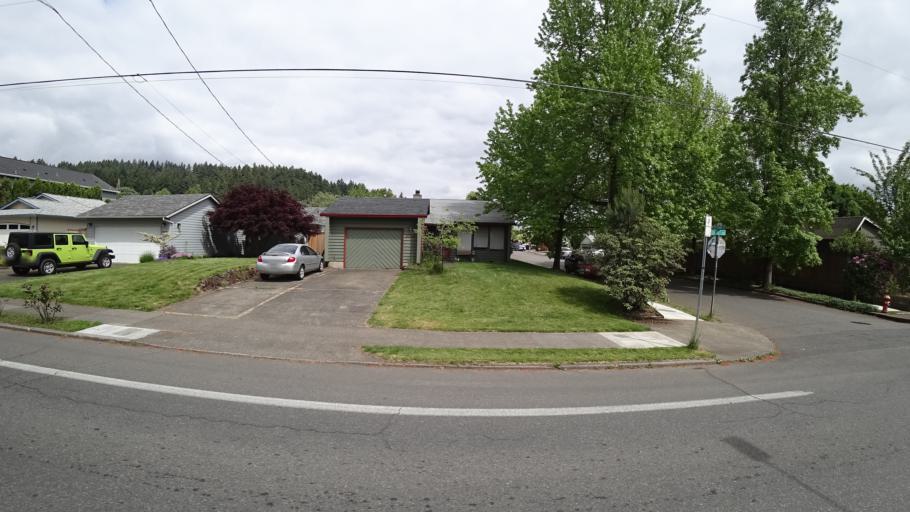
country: US
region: Oregon
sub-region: Multnomah County
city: Lents
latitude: 45.5076
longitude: -122.6017
